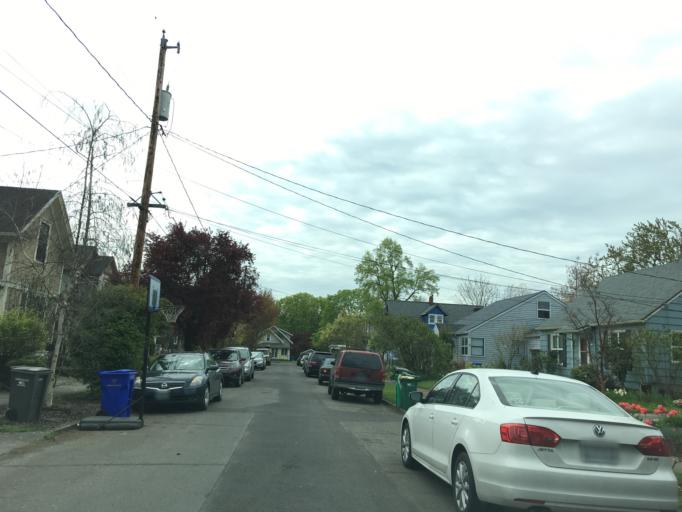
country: US
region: Oregon
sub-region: Multnomah County
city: Lents
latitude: 45.5282
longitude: -122.6012
